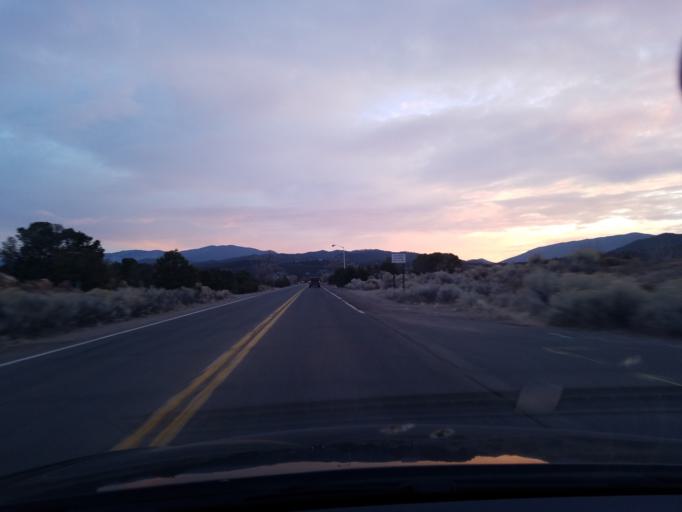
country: US
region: New Mexico
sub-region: Santa Fe County
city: Santa Fe
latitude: 35.6921
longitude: -105.9253
